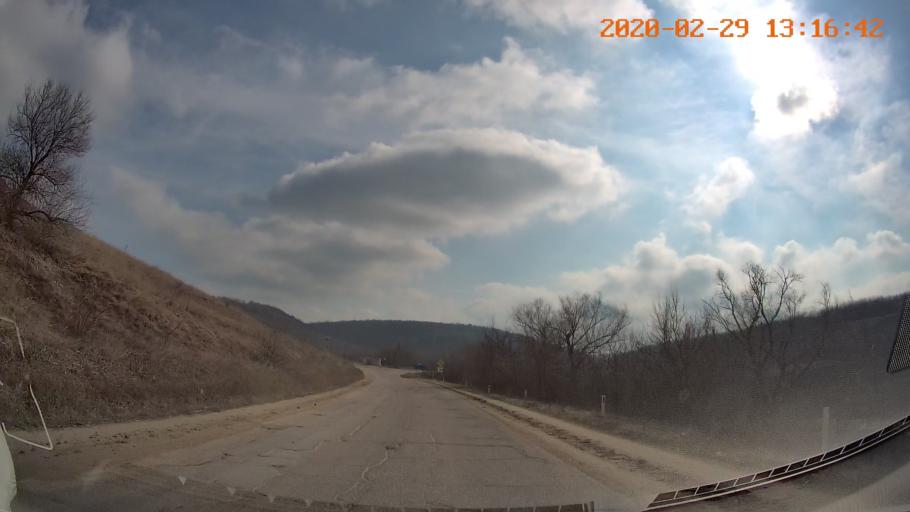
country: MD
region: Telenesti
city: Camenca
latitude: 48.0005
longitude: 28.6628
